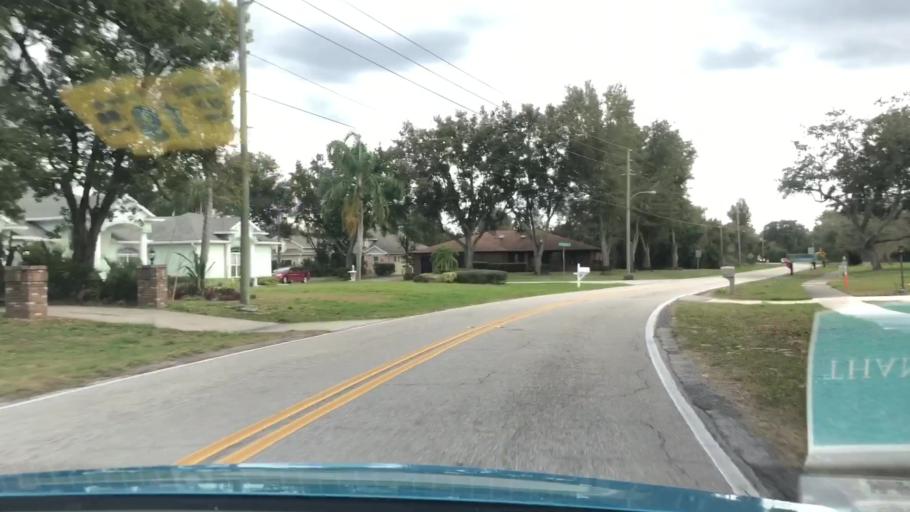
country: US
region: Florida
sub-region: Volusia County
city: Deltona
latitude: 28.8827
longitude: -81.2212
